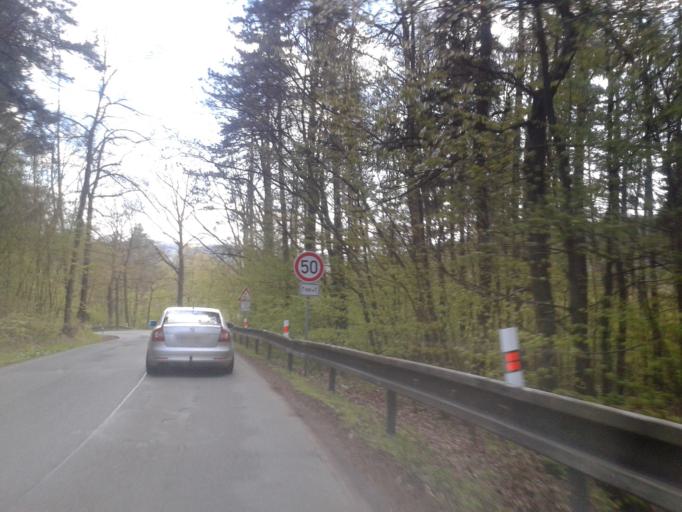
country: CZ
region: Central Bohemia
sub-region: Okres Beroun
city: Beroun
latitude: 49.9843
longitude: 14.0776
